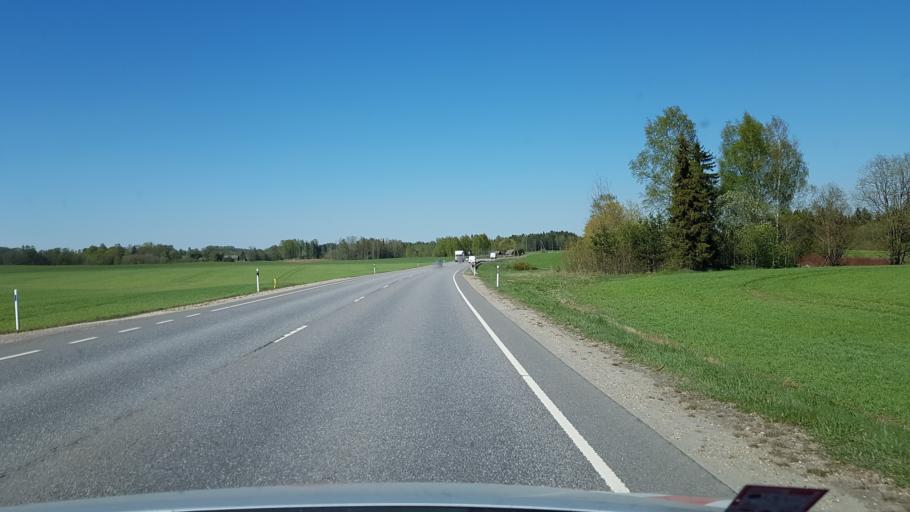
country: EE
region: Tartu
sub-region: UElenurme vald
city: Ulenurme
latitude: 58.0869
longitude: 26.7338
